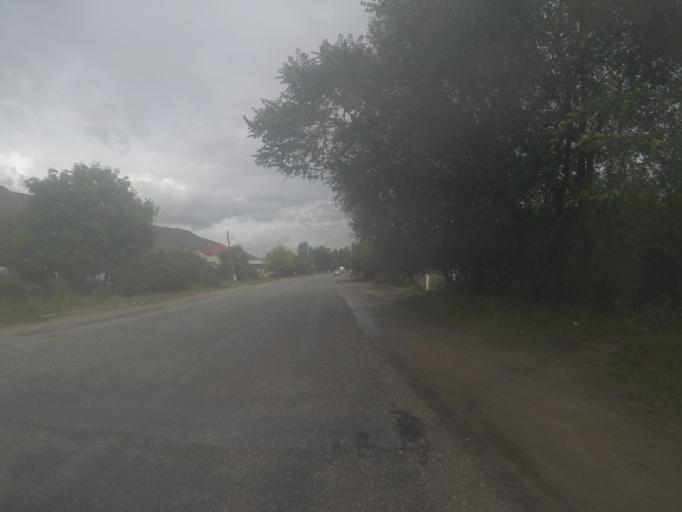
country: KG
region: Ysyk-Koel
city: Tyup
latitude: 42.7421
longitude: 78.0225
